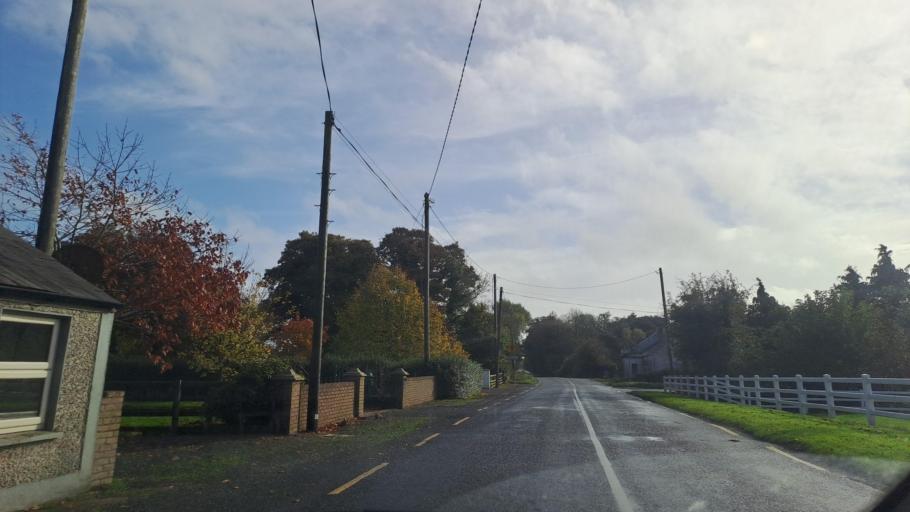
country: IE
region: Ulster
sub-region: County Monaghan
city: Carrickmacross
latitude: 53.9125
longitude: -6.7072
